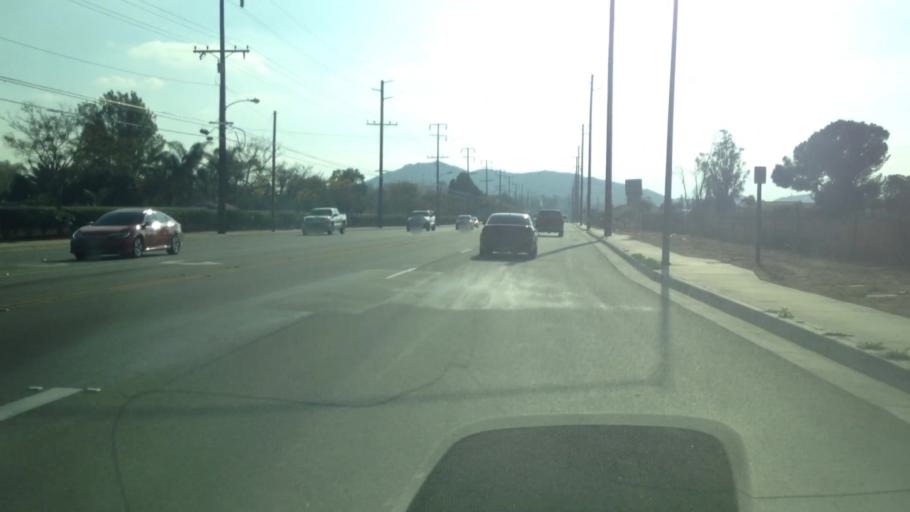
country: US
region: California
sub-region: Riverside County
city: Sunnyslope
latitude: 34.0214
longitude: -117.4238
